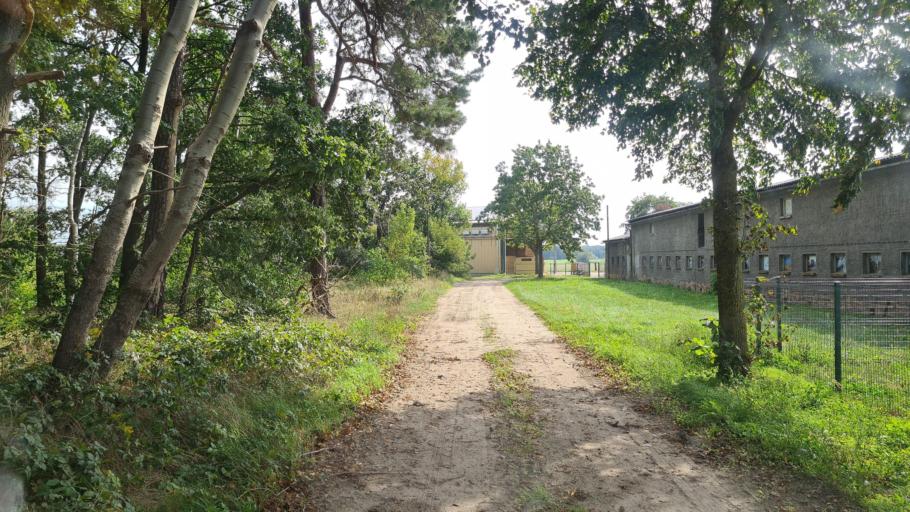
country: DE
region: Brandenburg
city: Sonnewalde
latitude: 51.7139
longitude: 13.6207
